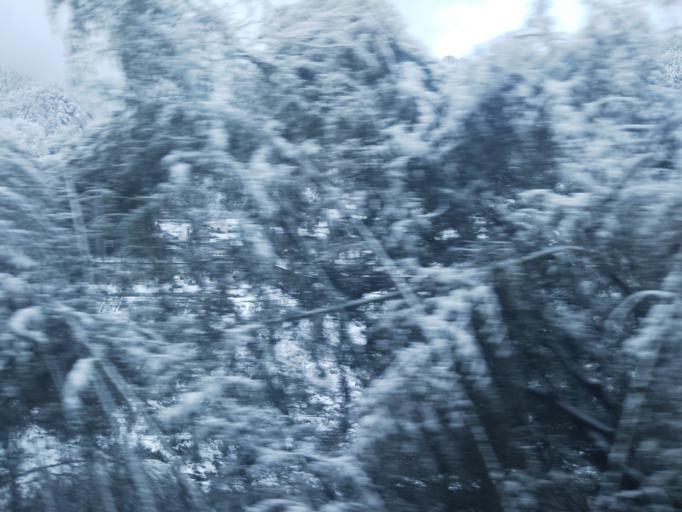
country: JP
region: Tokushima
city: Ikedacho
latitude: 33.7849
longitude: 133.7198
